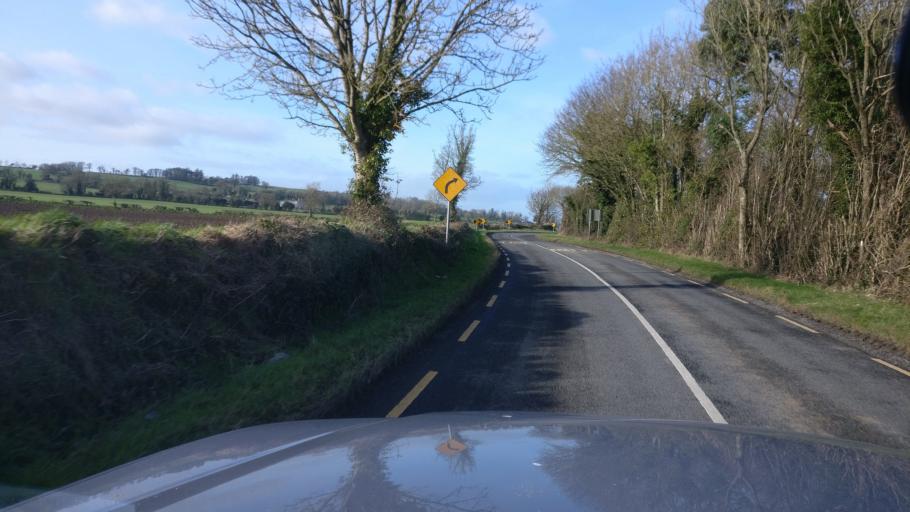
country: IE
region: Leinster
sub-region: Laois
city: Stradbally
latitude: 52.9976
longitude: -7.2236
